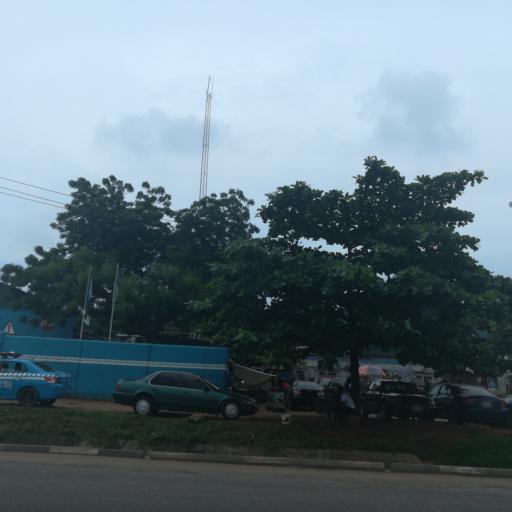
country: NG
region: Lagos
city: Ojota
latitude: 6.6023
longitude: 3.3760
